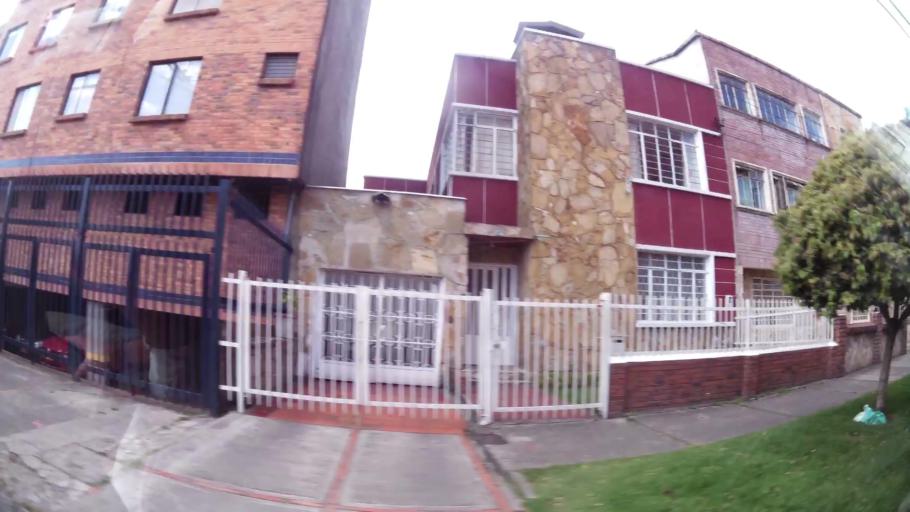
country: CO
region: Bogota D.C.
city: Bogota
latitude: 4.6468
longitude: -74.0702
